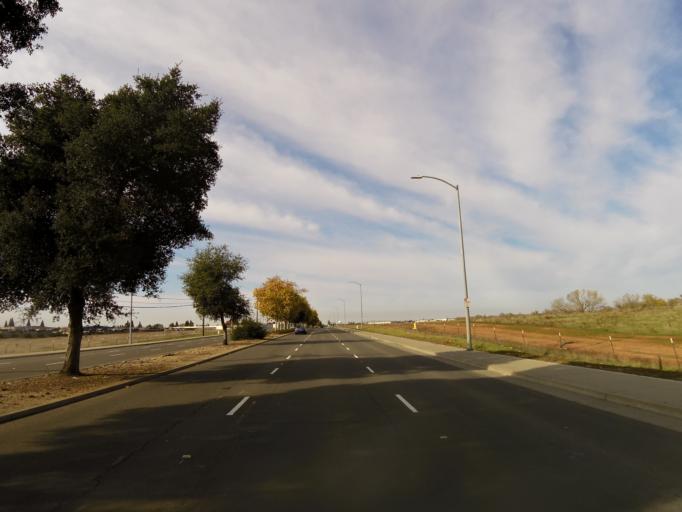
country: US
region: California
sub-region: Sacramento County
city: Rancho Cordova
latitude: 38.5640
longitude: -121.2473
